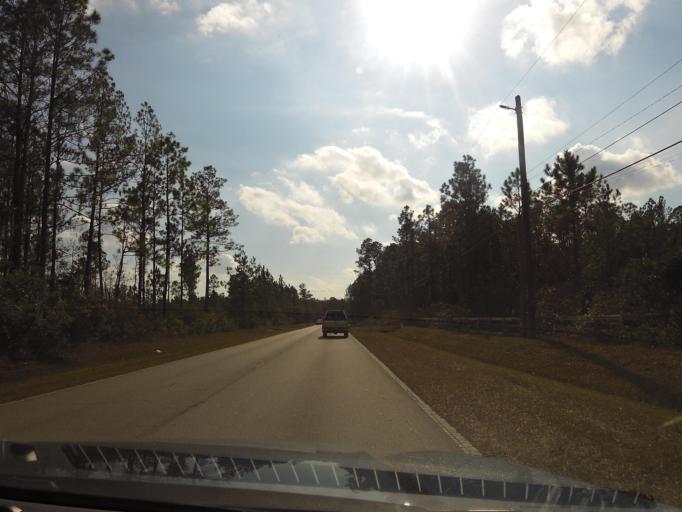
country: US
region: Florida
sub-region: Duval County
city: Baldwin
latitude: 30.1893
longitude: -81.9911
